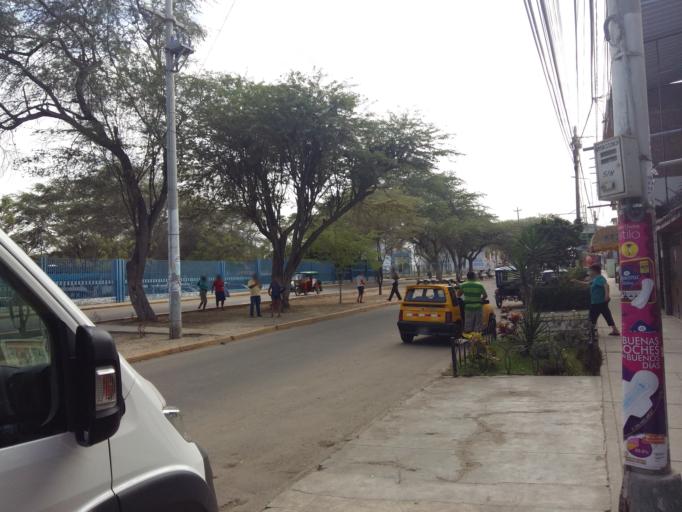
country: PE
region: Piura
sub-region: Provincia de Piura
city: Piura
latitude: -5.1882
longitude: -80.6225
